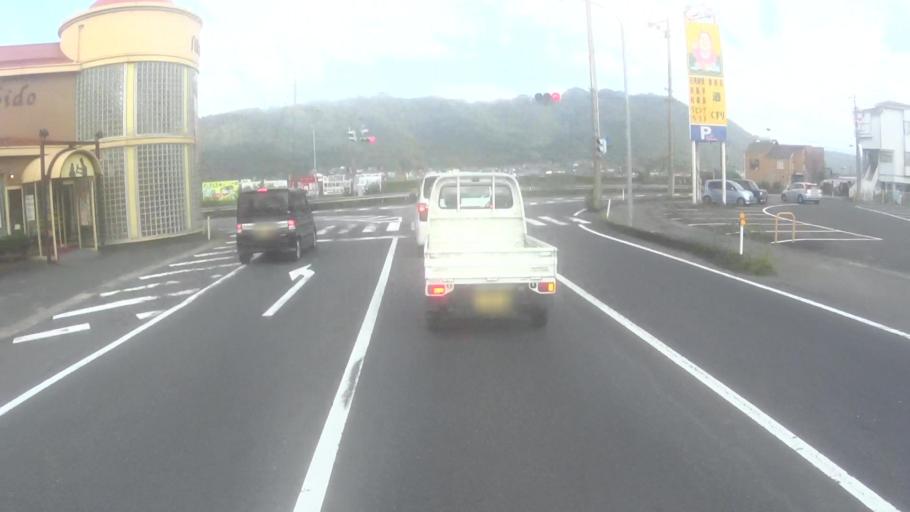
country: JP
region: Kyoto
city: Miyazu
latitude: 35.5345
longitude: 135.1225
